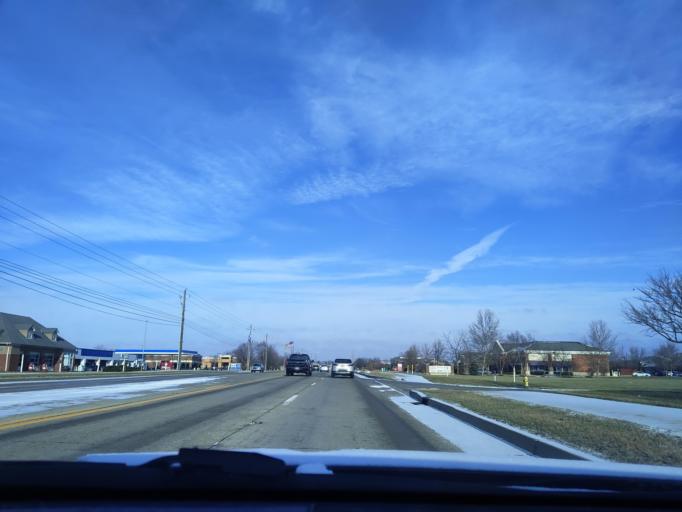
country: US
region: Indiana
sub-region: Boone County
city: Zionsville
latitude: 39.9363
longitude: -86.2345
